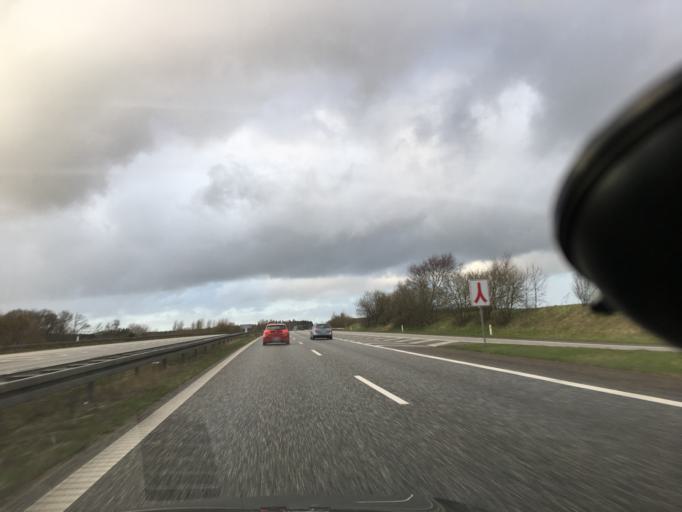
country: DK
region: North Denmark
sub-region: Mariagerfjord Kommune
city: Hobro
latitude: 56.6264
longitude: 9.7332
